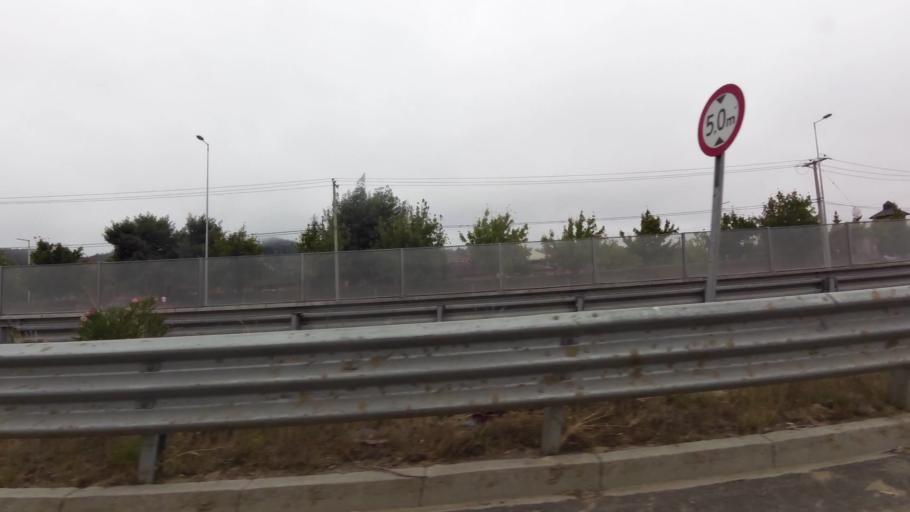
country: CL
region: Biobio
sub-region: Provincia de Concepcion
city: Concepcion
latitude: -36.8191
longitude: -73.0064
